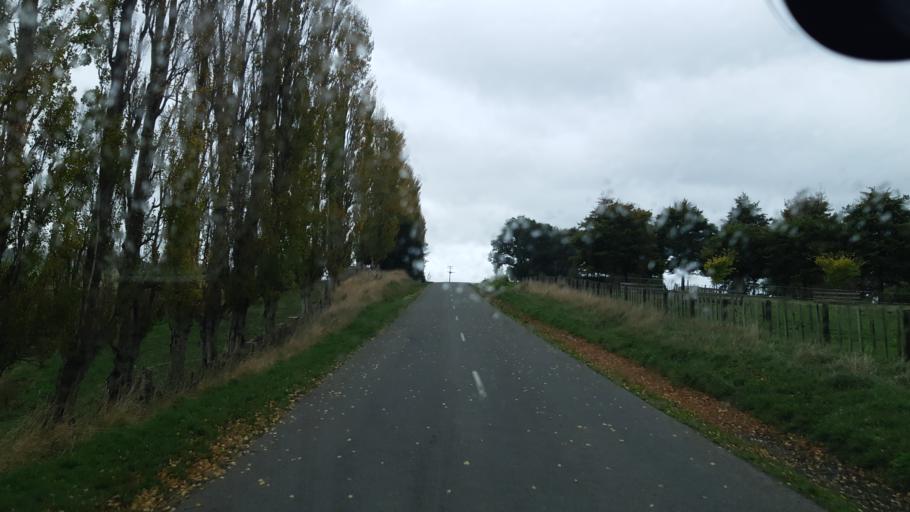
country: NZ
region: Manawatu-Wanganui
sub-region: Ruapehu District
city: Waiouru
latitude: -39.6208
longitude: 175.6254
